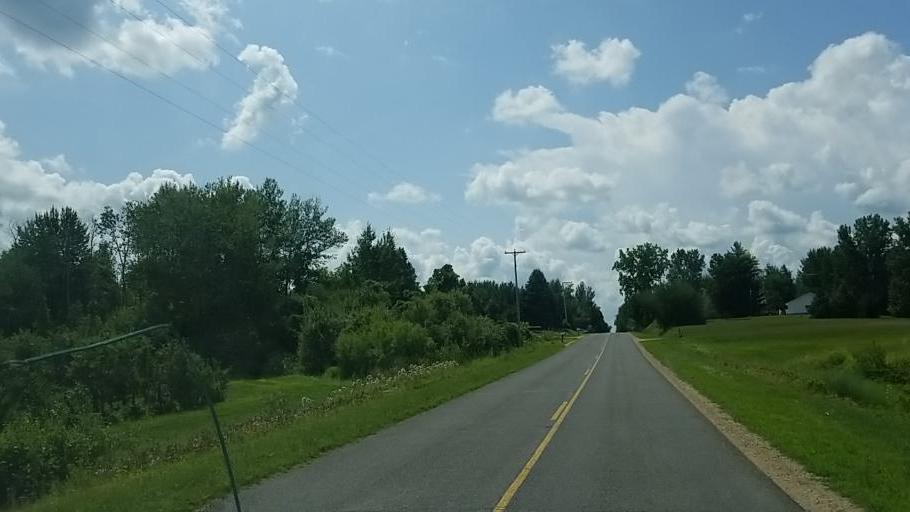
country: US
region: Michigan
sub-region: Muskegon County
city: Ravenna
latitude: 43.2301
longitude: -85.8798
